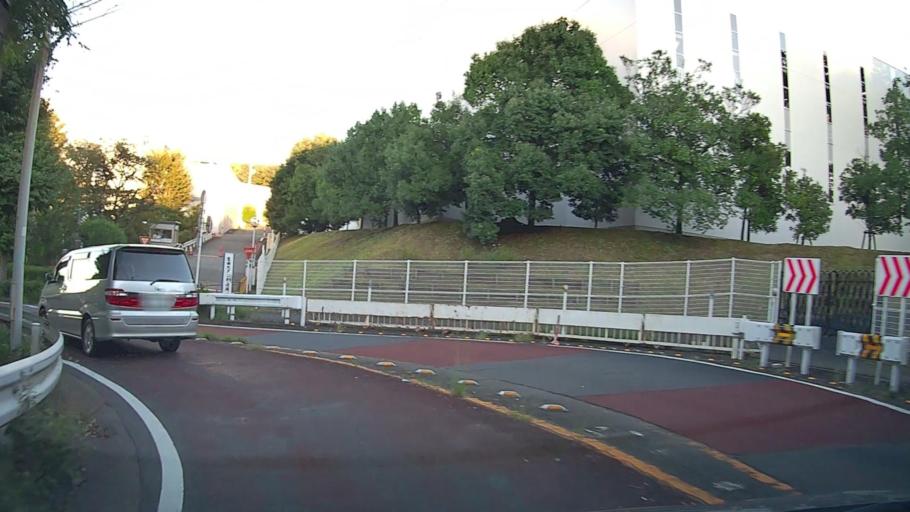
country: JP
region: Tokyo
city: Chofugaoka
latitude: 35.6216
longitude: 139.5245
